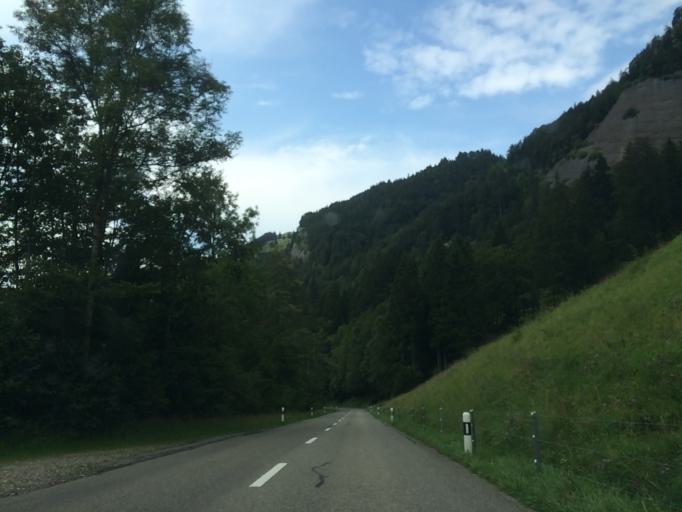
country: CH
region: Appenzell Ausserrhoden
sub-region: Bezirk Hinterland
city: Urnasch
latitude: 47.2438
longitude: 9.2628
